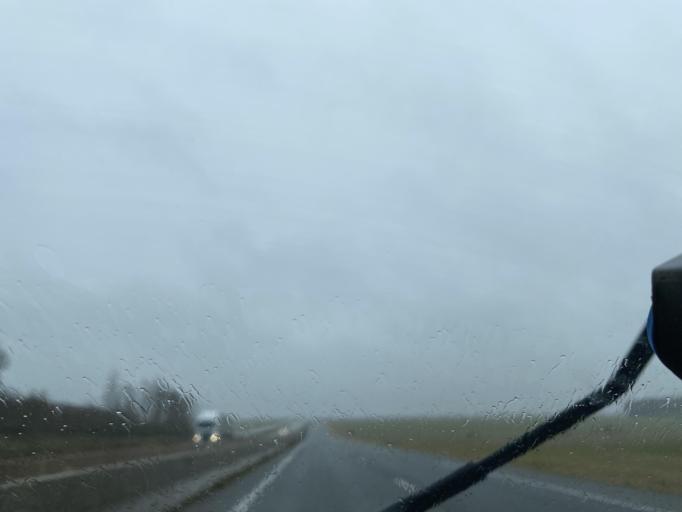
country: FR
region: Centre
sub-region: Departement d'Eure-et-Loir
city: Bailleau-l'Eveque
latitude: 48.5748
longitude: 1.4337
